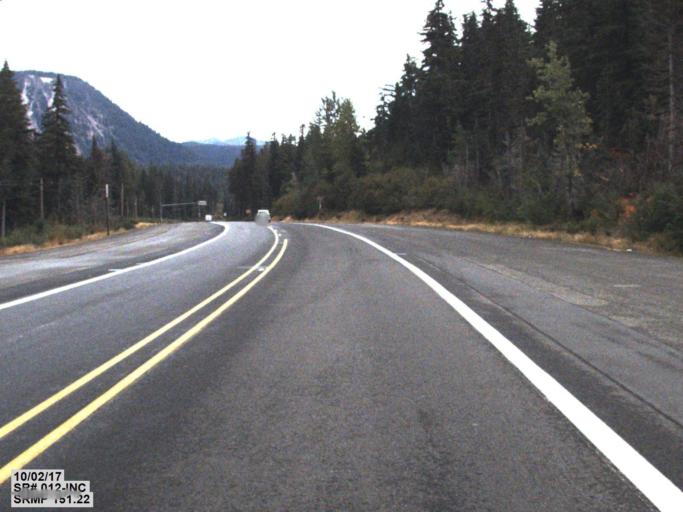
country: US
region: Washington
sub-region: Yakima County
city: Tieton
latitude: 46.6392
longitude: -121.3880
